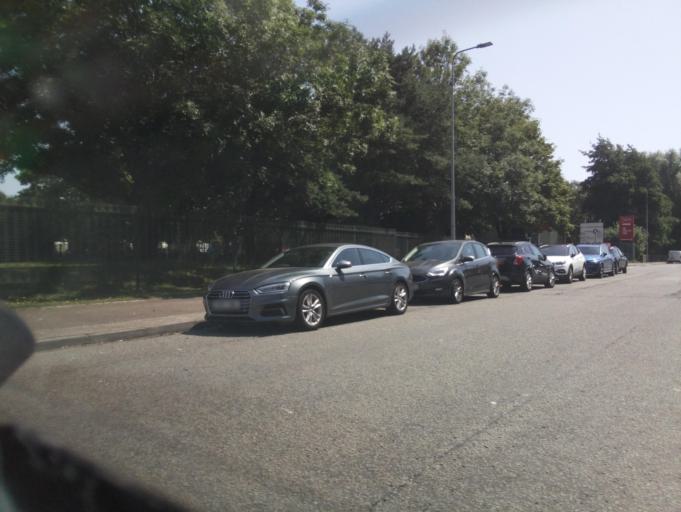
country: GB
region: Wales
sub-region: Cardiff
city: Cardiff
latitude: 51.4753
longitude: -3.1470
